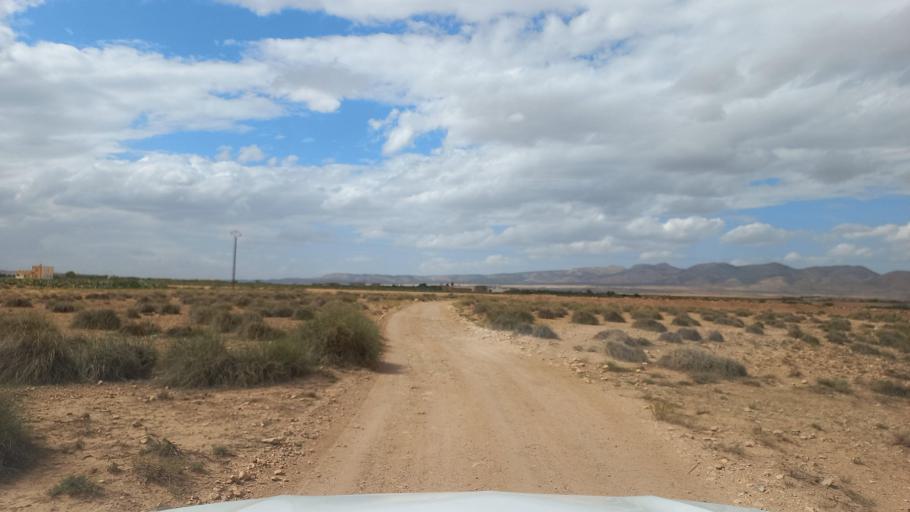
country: TN
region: Al Qasrayn
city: Sbiba
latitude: 35.3815
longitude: 9.0996
